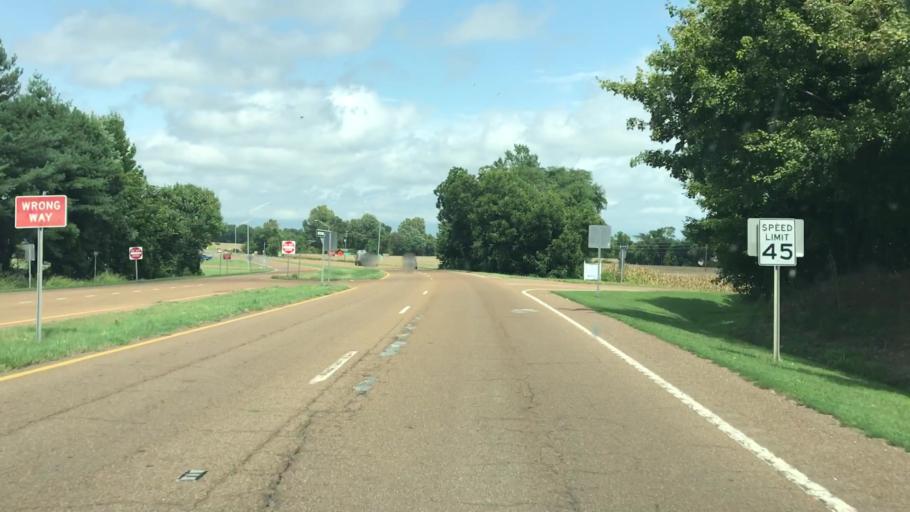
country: US
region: Tennessee
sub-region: Obion County
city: Troy
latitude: 36.3359
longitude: -89.1592
